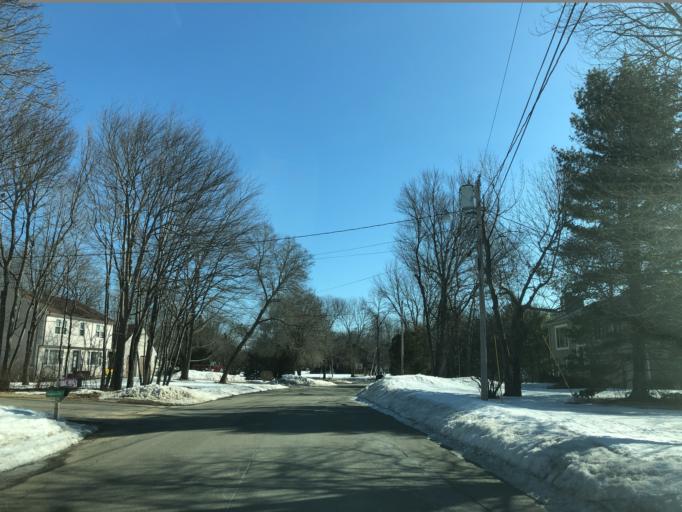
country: US
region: Maine
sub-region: Penobscot County
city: Brewer
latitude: 44.8204
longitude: -68.7518
